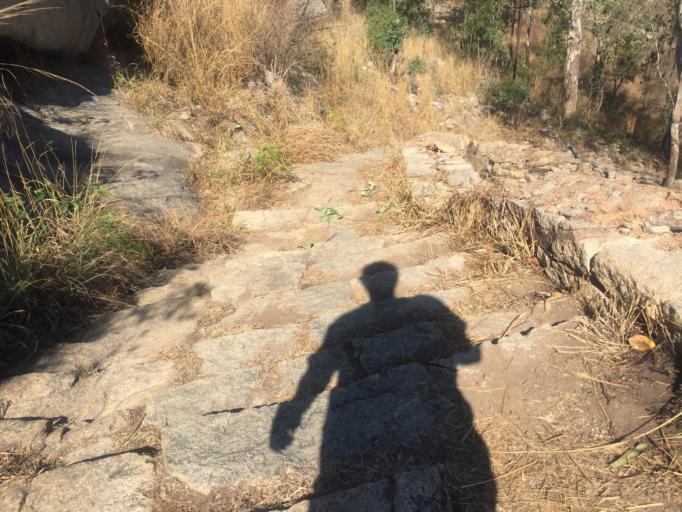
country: IN
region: Karnataka
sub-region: Chikkaballapur
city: Chik Ballapur
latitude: 13.3746
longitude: 77.6759
